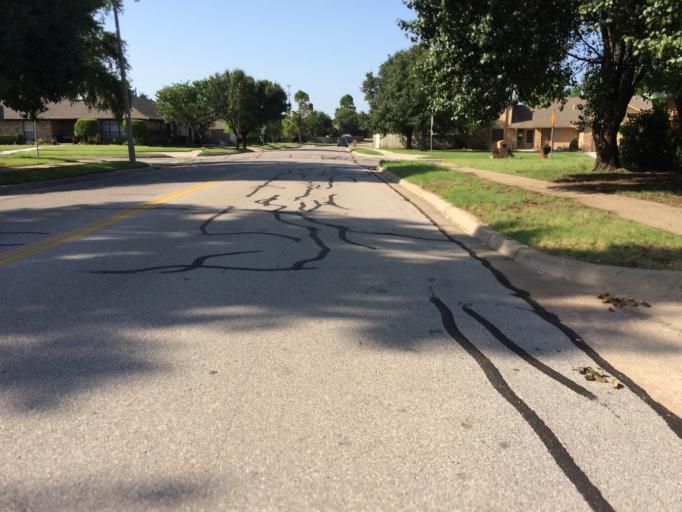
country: US
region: Oklahoma
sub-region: Cleveland County
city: Norman
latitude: 35.2393
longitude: -97.4888
